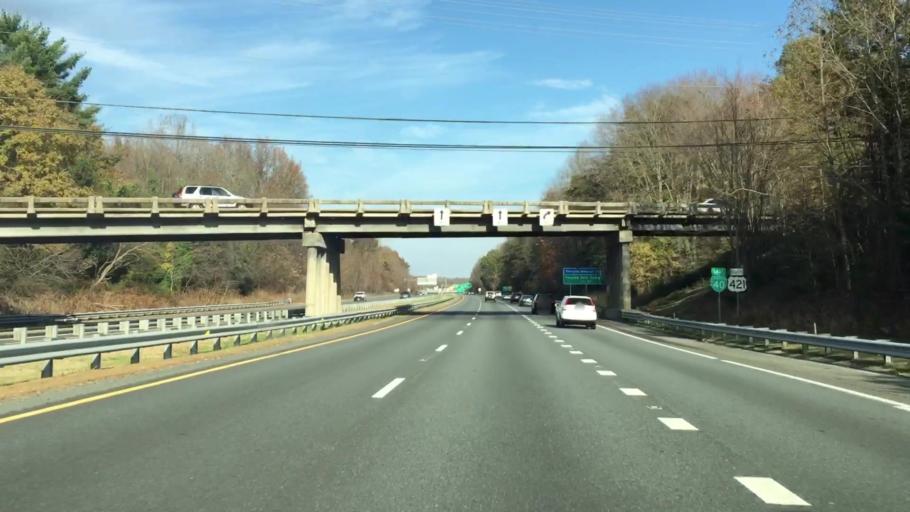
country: US
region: North Carolina
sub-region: Forsyth County
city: Winston-Salem
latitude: 36.0772
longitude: -80.3170
